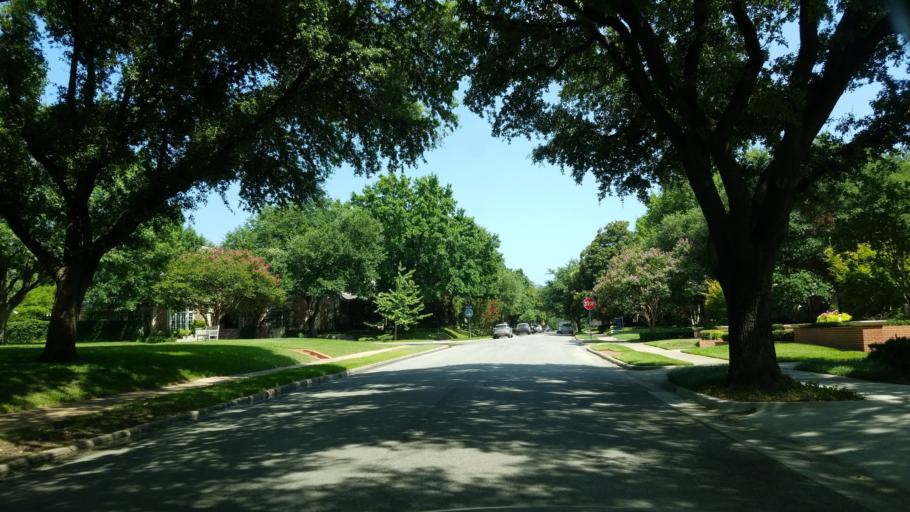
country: US
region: Texas
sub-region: Dallas County
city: Highland Park
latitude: 32.8278
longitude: -96.7921
